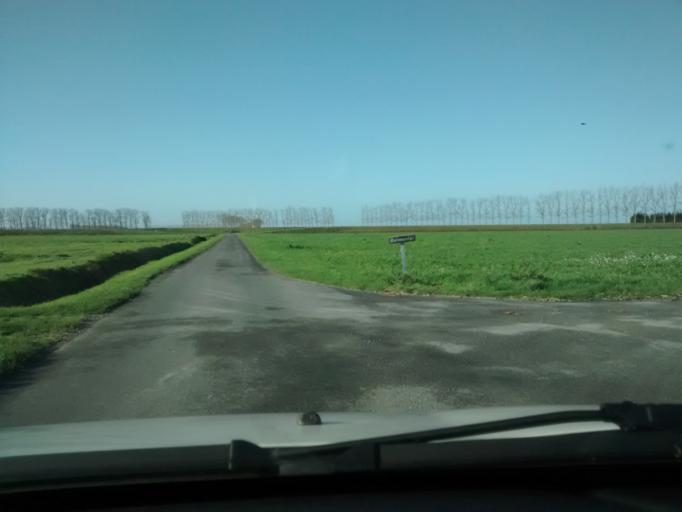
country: FR
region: Brittany
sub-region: Departement d'Ille-et-Vilaine
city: Roz-sur-Couesnon
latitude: 48.6183
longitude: -1.5446
